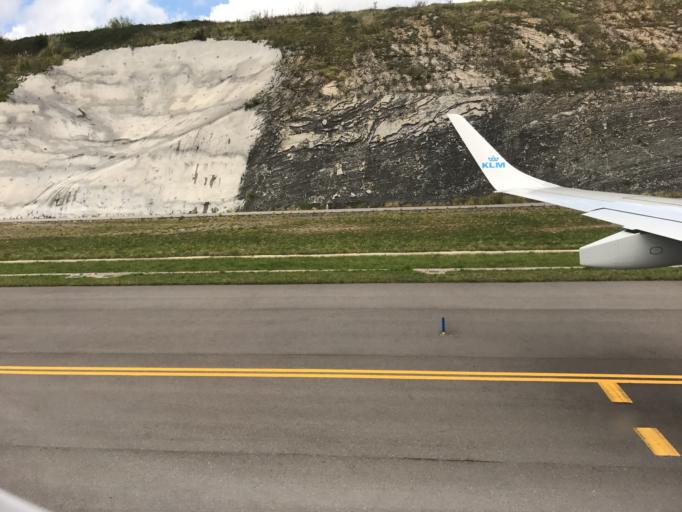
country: ES
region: Basque Country
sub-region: Bizkaia
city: Sondika
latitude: 43.3063
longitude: -2.9195
